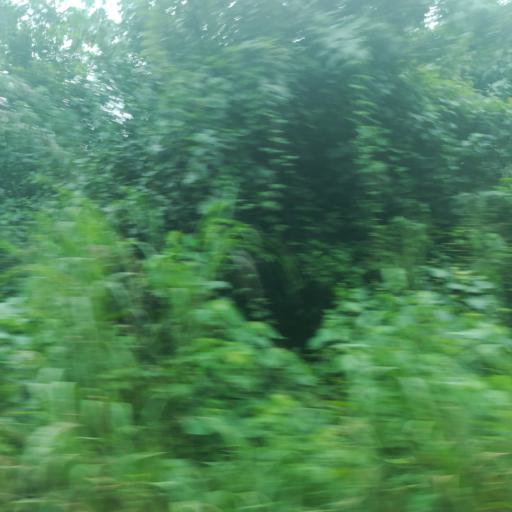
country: NG
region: Lagos
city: Ejirin
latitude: 6.6474
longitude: 3.7505
